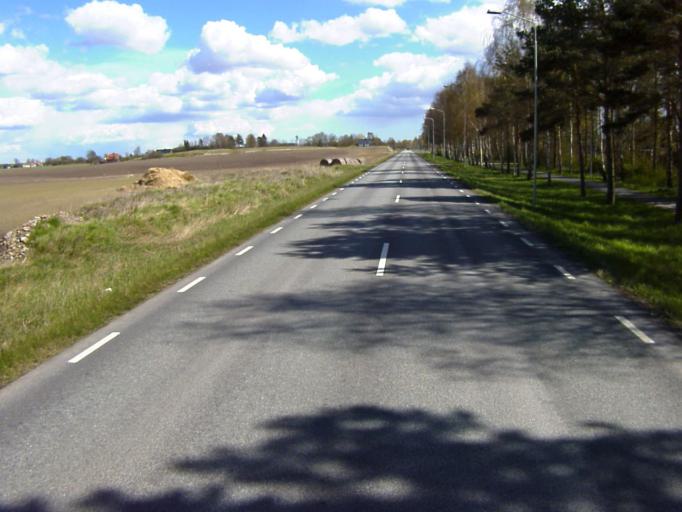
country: SE
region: Skane
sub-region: Kristianstads Kommun
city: Kristianstad
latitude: 56.0165
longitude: 14.0951
